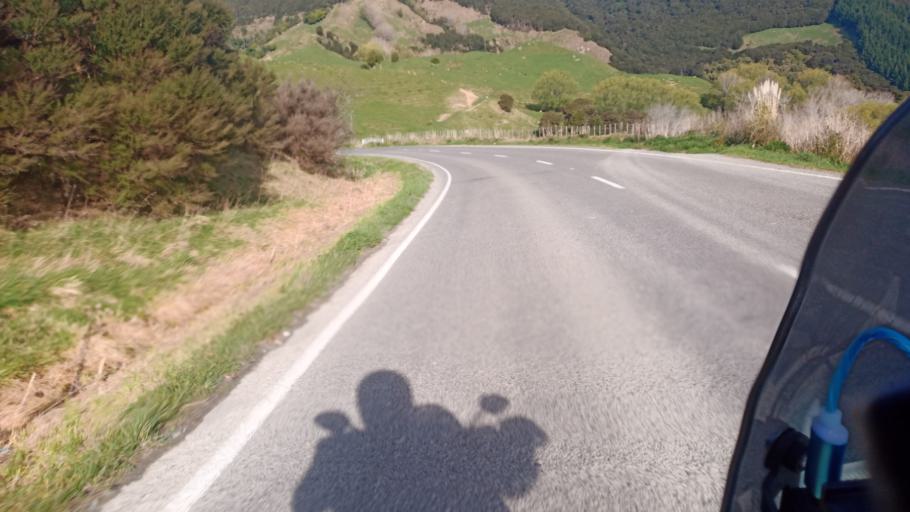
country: NZ
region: Gisborne
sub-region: Gisborne District
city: Gisborne
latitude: -38.1544
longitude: 178.2845
